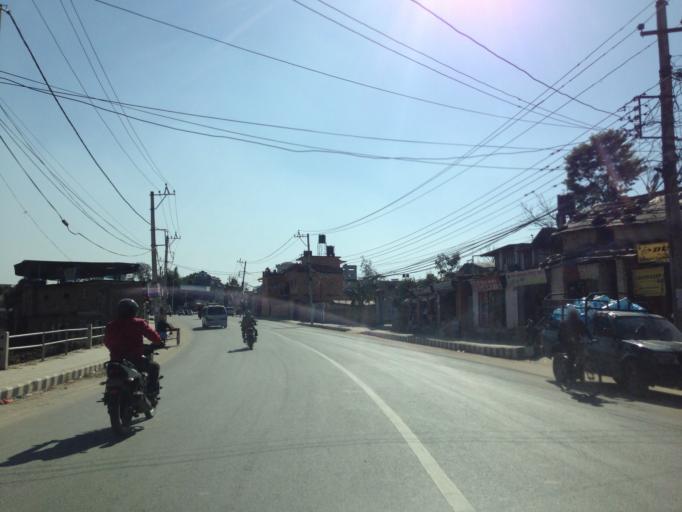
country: NP
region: Central Region
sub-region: Bagmati Zone
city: Kathmandu
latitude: 27.7505
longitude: 85.3457
